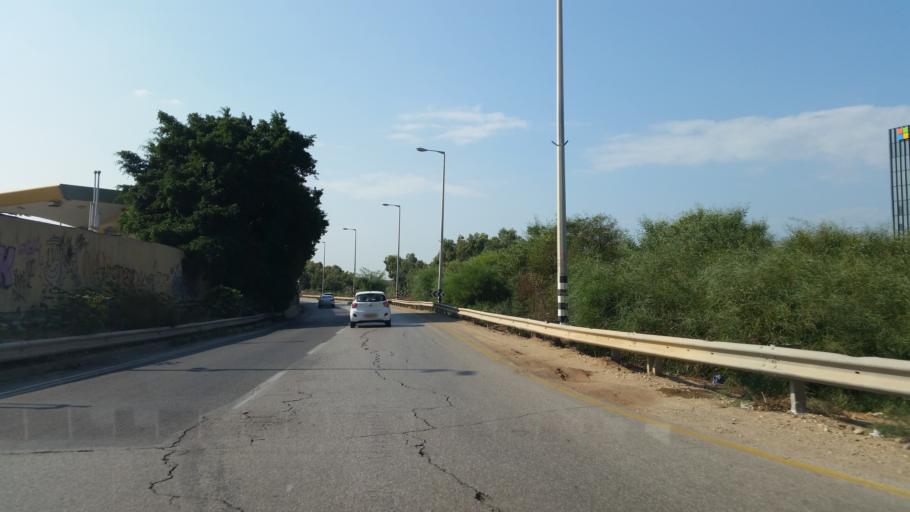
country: IL
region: Tel Aviv
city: Herzliya Pituah
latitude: 32.1567
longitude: 34.8082
